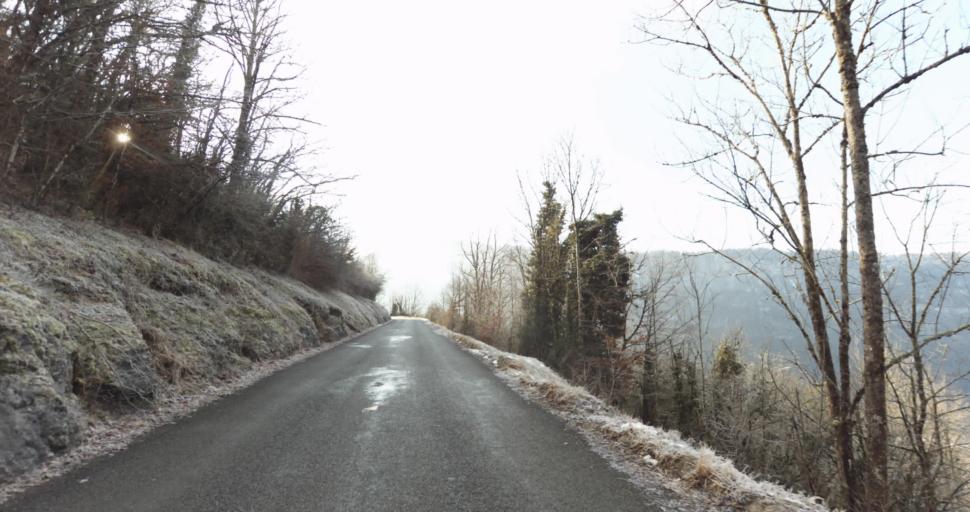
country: FR
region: Rhone-Alpes
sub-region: Departement de l'Ain
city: Nantua
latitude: 46.1510
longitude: 5.6171
